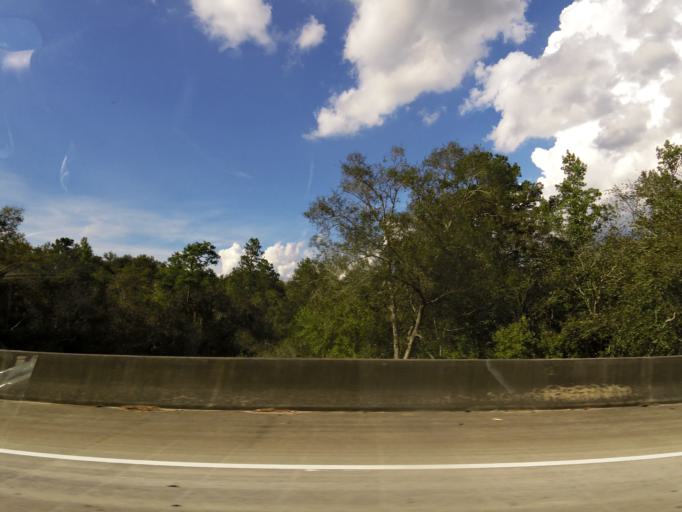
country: US
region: Georgia
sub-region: Brooks County
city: Quitman
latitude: 30.7936
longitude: -83.4531
